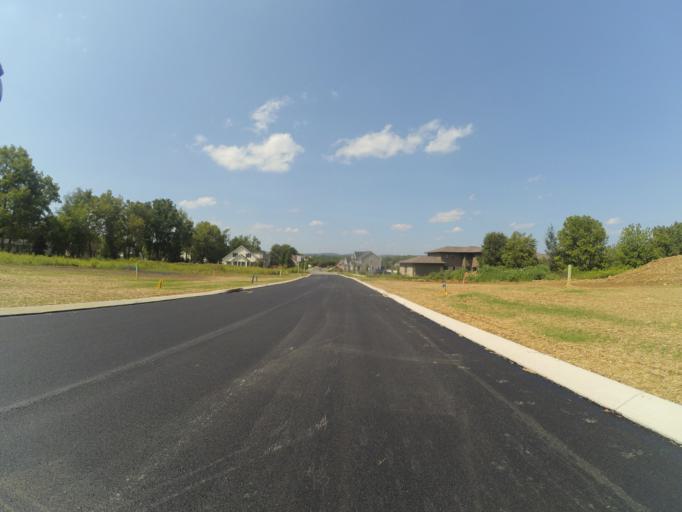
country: US
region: Pennsylvania
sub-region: Centre County
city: Houserville
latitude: 40.8283
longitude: -77.8226
